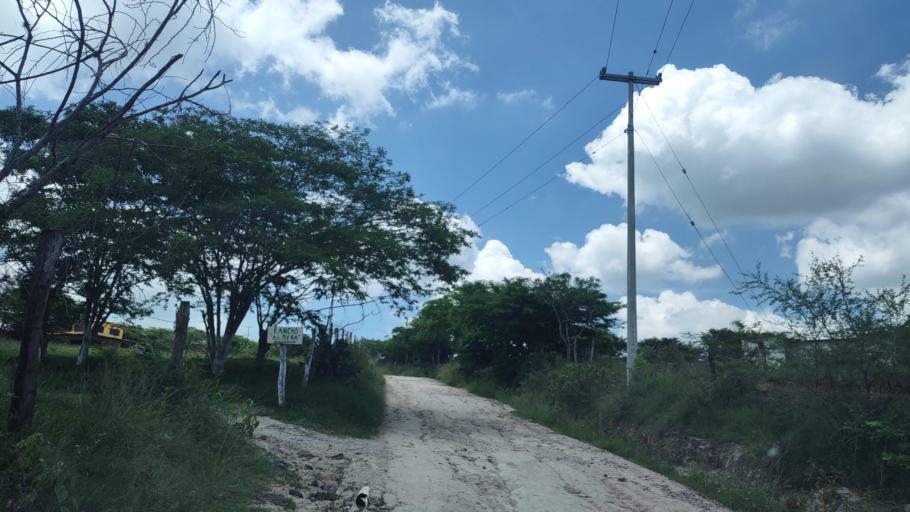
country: MX
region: Veracruz
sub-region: Emiliano Zapata
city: Dos Rios
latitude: 19.4996
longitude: -96.8126
